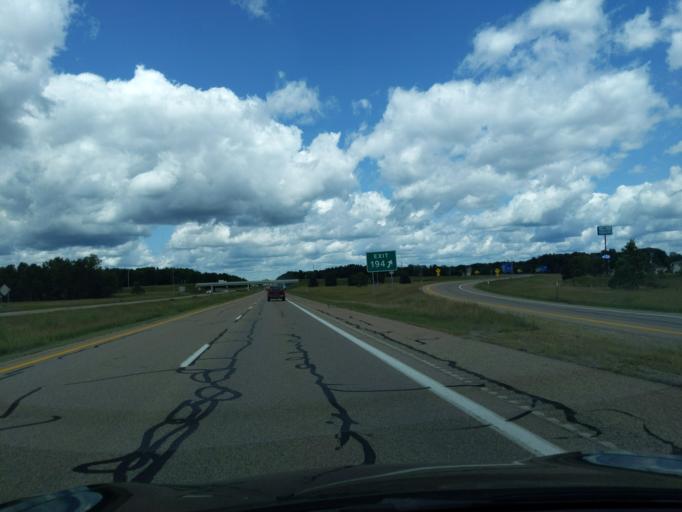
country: US
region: Michigan
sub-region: Roscommon County
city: Houghton Lake
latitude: 44.3323
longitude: -84.8071
